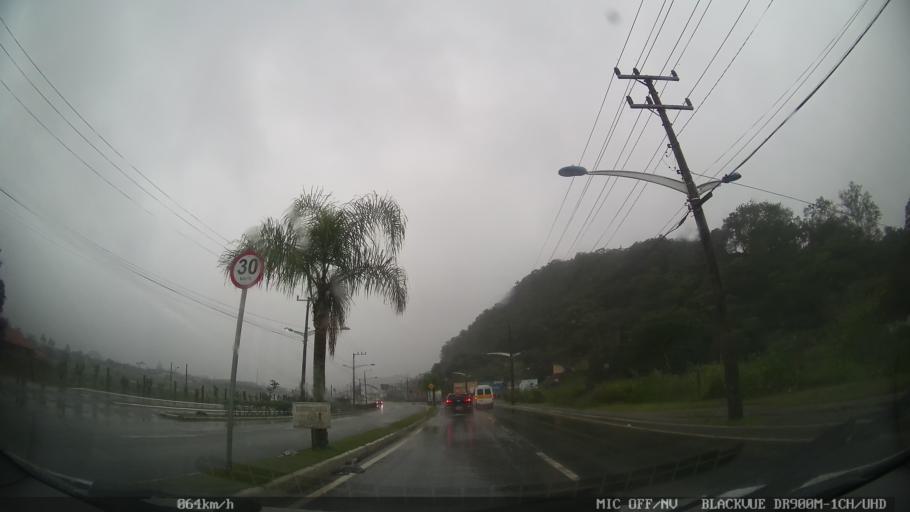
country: BR
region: Santa Catarina
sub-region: Itajai
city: Itajai
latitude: -26.9362
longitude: -48.6948
